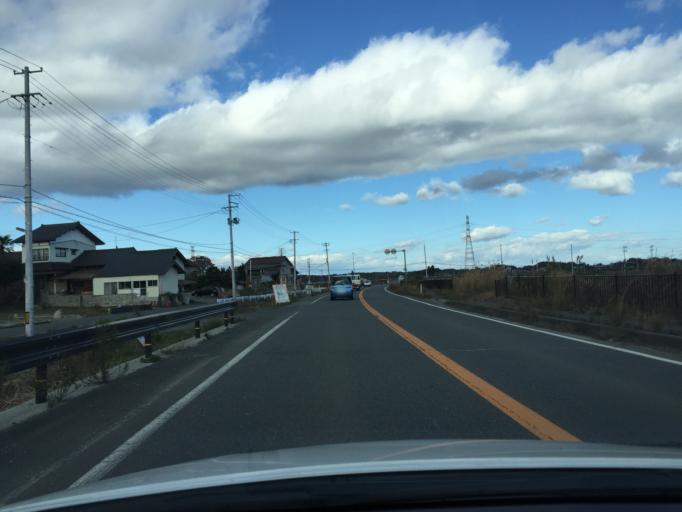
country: JP
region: Fukushima
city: Namie
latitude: 37.5894
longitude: 141.0058
